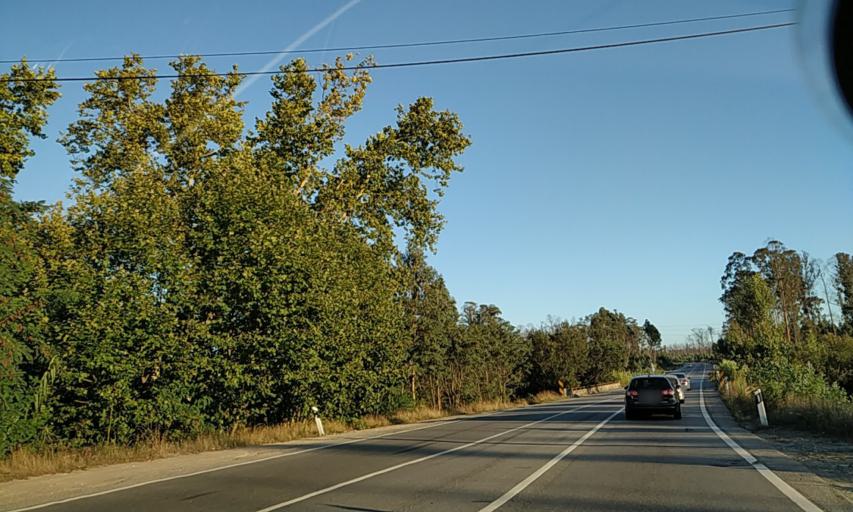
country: PT
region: Aveiro
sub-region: Oliveira do Bairro
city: Oia
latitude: 40.5647
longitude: -8.5638
